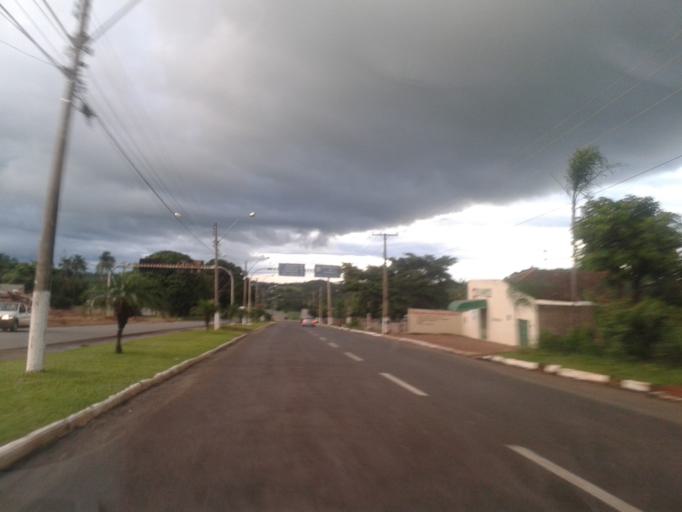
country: BR
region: Goias
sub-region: Morrinhos
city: Morrinhos
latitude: -17.7293
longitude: -49.1509
